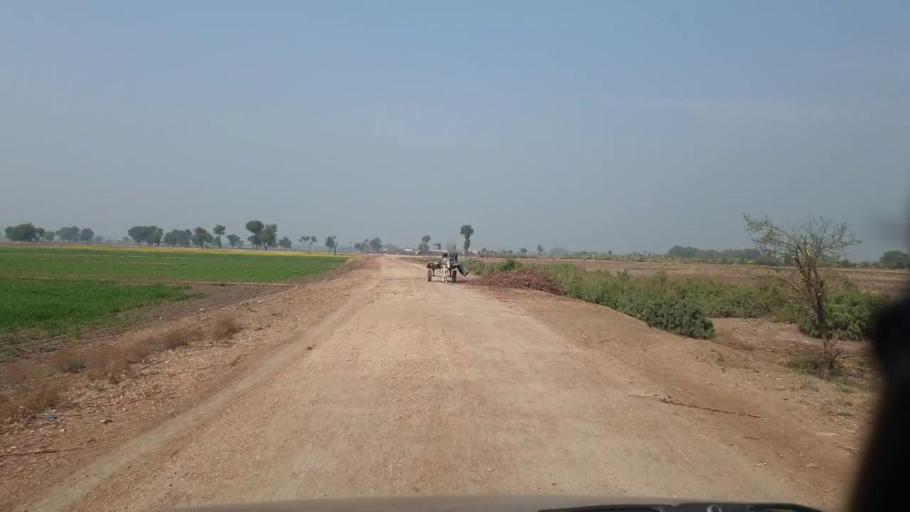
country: PK
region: Sindh
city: Shahdadpur
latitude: 26.0356
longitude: 68.5034
